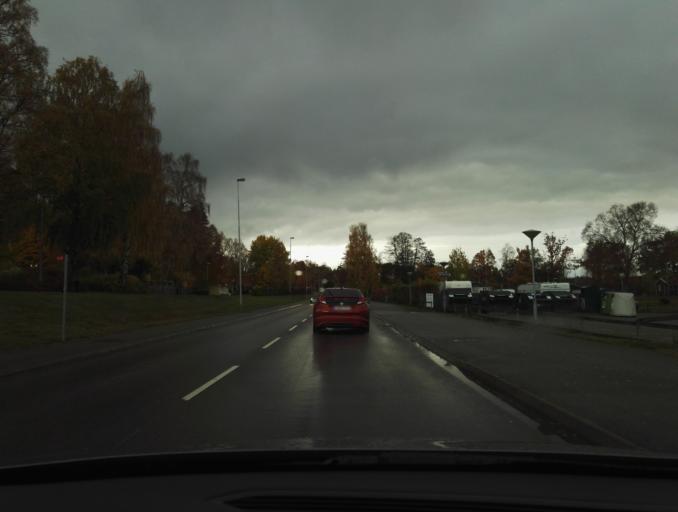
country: SE
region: Kronoberg
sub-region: Vaxjo Kommun
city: Vaexjoe
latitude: 56.9003
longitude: 14.7389
